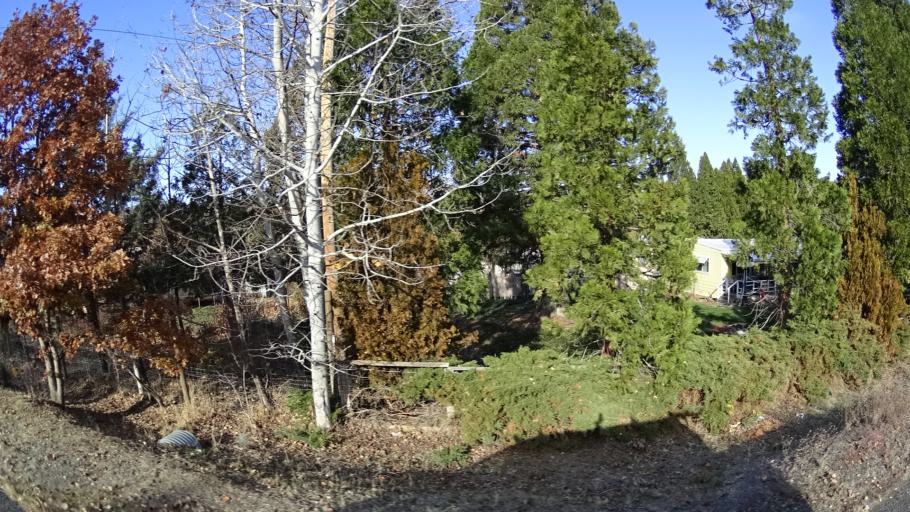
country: US
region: California
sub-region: Siskiyou County
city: Yreka
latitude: 41.6984
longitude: -122.6329
